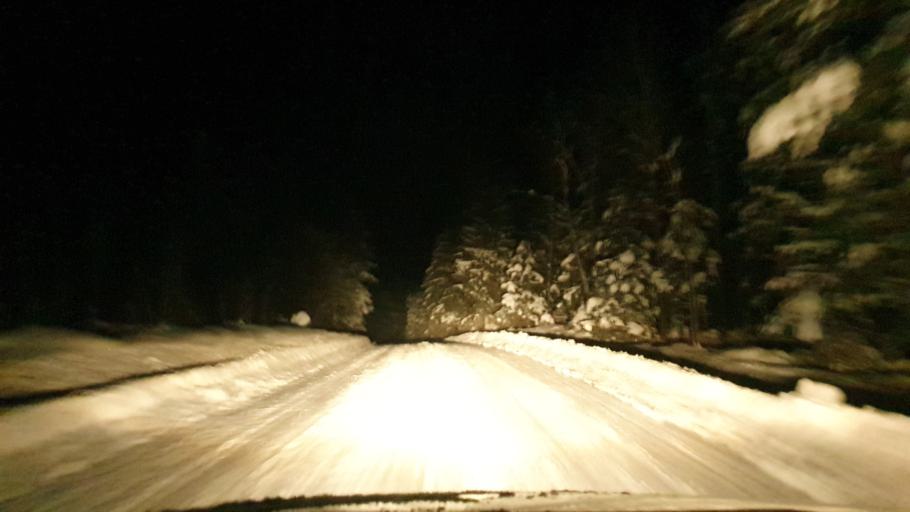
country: EE
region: Vorumaa
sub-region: Antsla vald
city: Vana-Antsla
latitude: 57.9477
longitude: 26.6280
